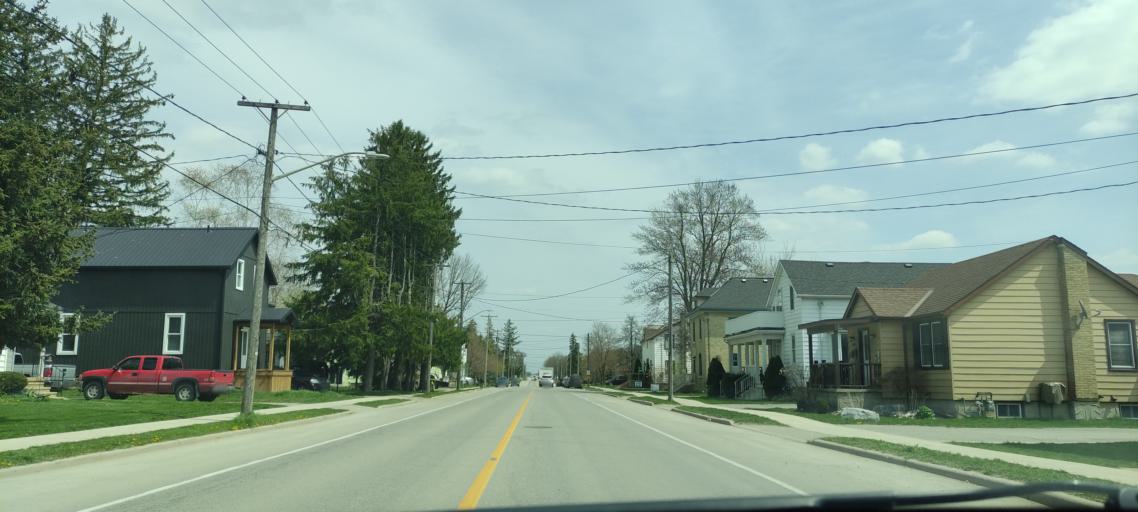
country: CA
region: Ontario
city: Stratford
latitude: 43.3225
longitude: -80.8314
